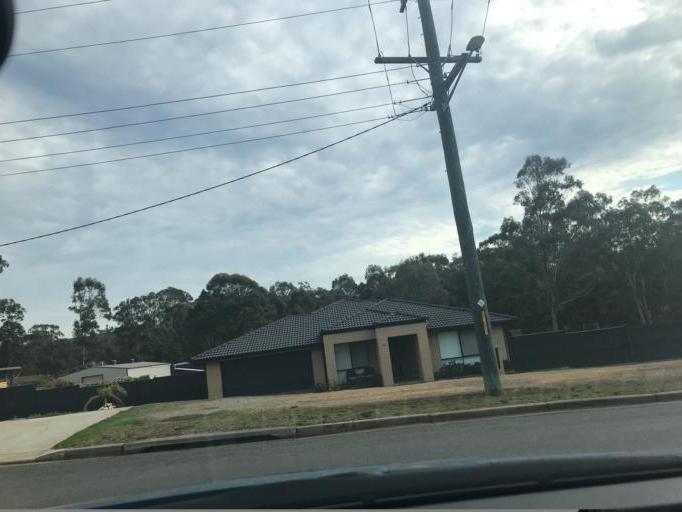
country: AU
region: New South Wales
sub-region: Cessnock
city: Cessnock
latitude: -32.9020
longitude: 151.2860
